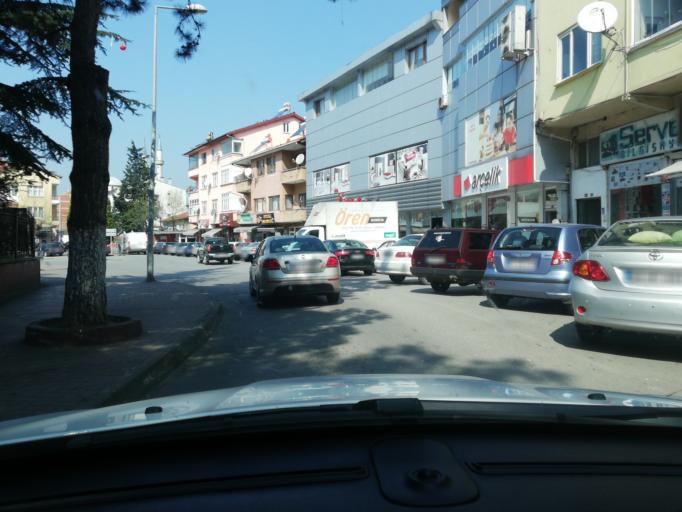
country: TR
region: Karabuk
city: Yenice
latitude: 41.2009
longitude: 32.3287
